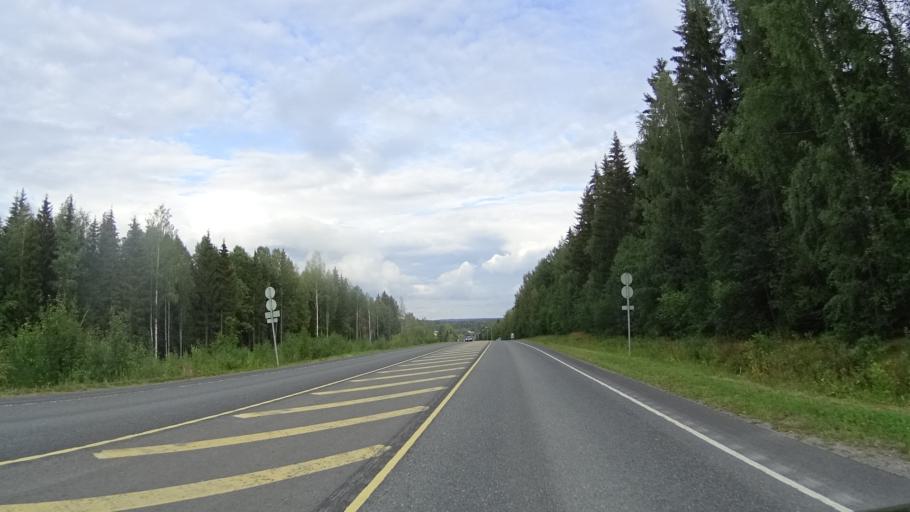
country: FI
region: Haeme
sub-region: Haemeenlinna
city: Parola
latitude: 61.0256
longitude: 24.3077
